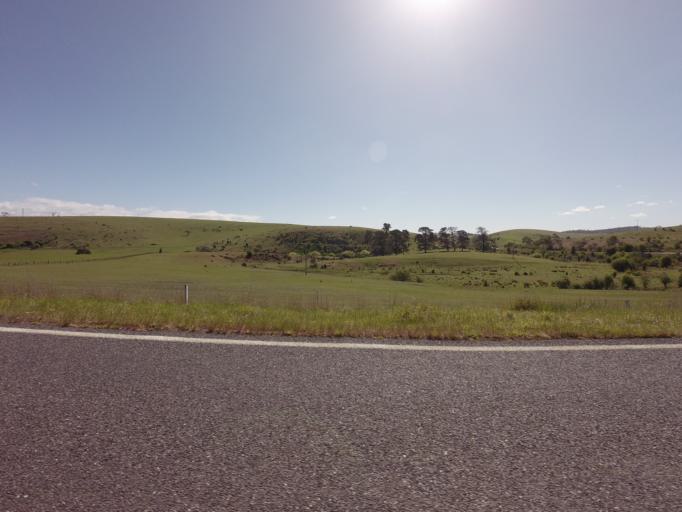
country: AU
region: Tasmania
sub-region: Derwent Valley
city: New Norfolk
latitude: -42.6547
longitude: 146.9354
